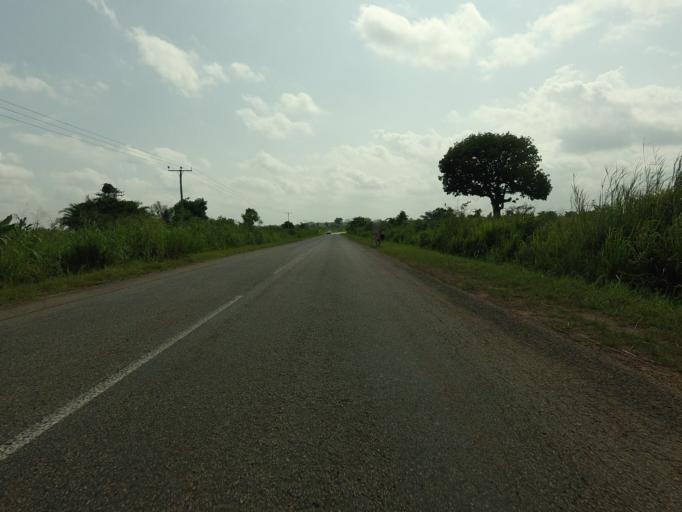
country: TG
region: Maritime
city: Tsevie
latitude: 6.3929
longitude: 0.8147
